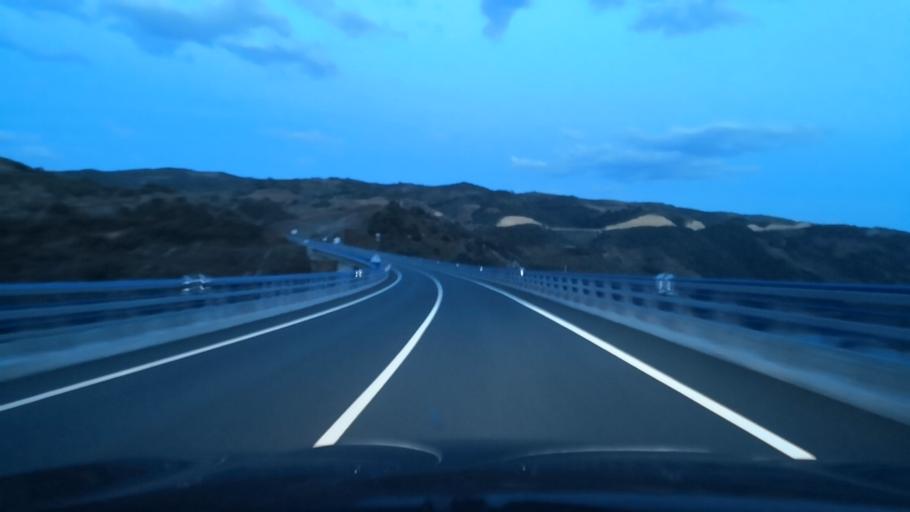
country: PT
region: Braganca
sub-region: Alfandega da Fe
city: Alfandega da Fe
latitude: 41.3078
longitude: -6.9208
